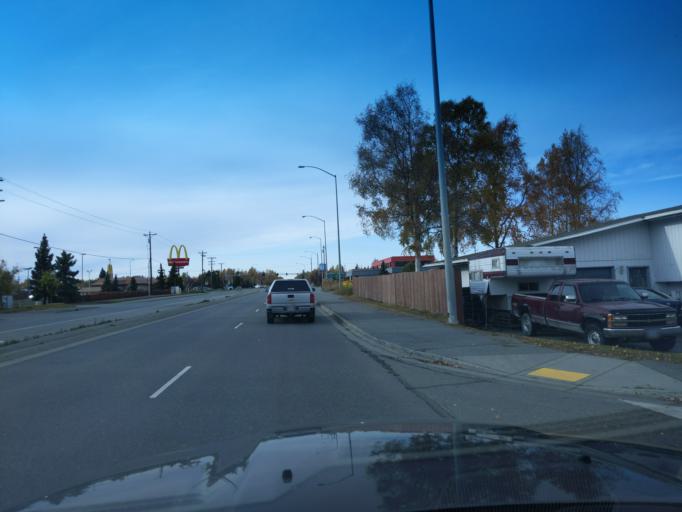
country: US
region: Alaska
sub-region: Anchorage Municipality
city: Anchorage
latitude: 61.1376
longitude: -149.9472
